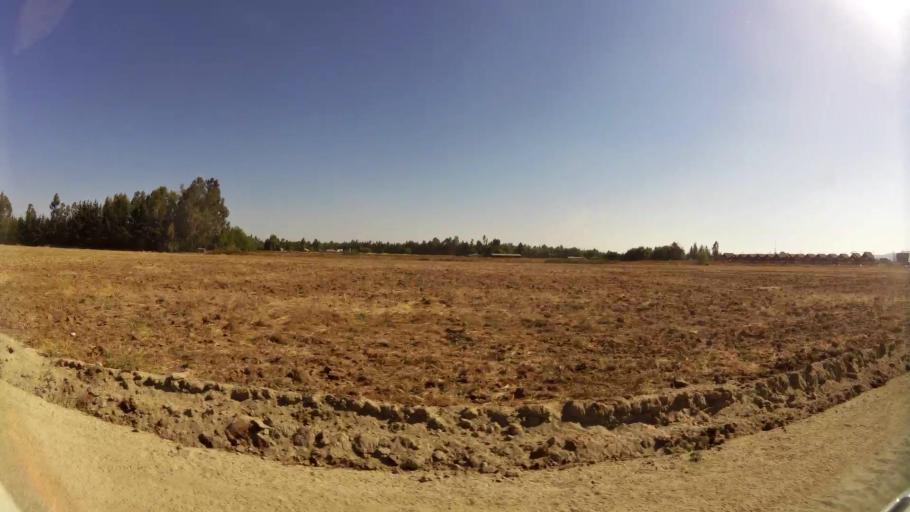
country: CL
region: Maule
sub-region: Provincia de Talca
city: Talca
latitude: -35.4159
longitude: -71.5986
